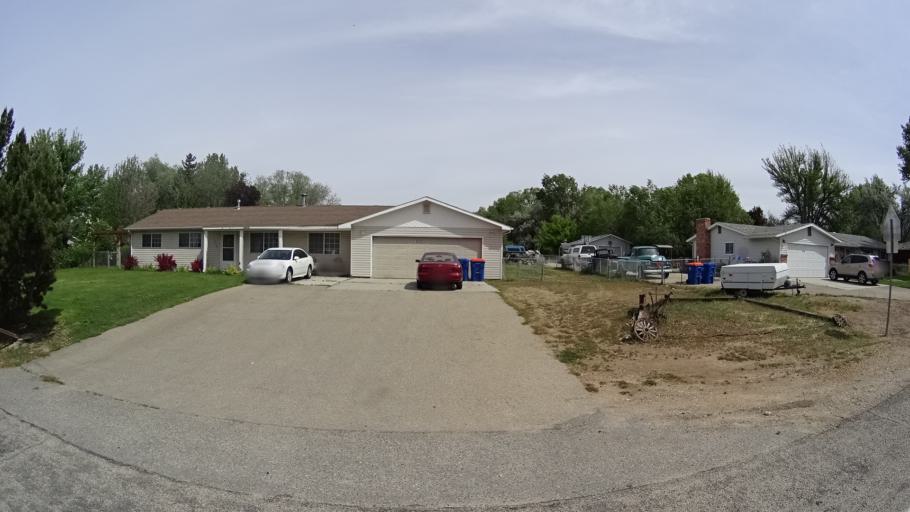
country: US
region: Idaho
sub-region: Ada County
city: Meridian
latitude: 43.5539
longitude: -116.3221
